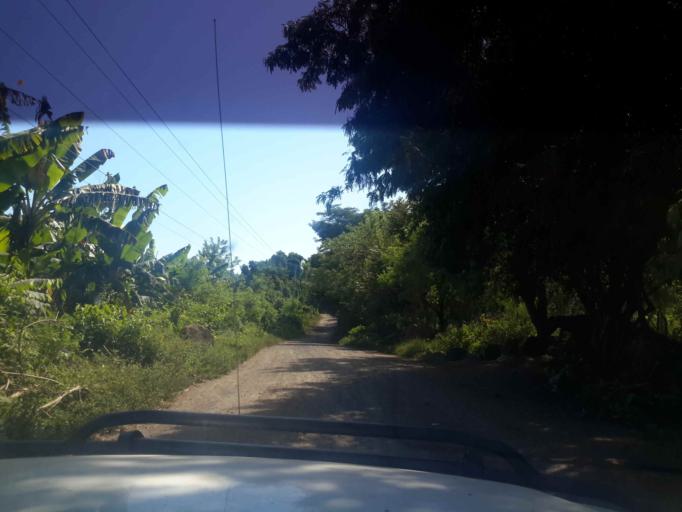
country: NI
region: Rivas
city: Altagracia
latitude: 11.4687
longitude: -85.4646
